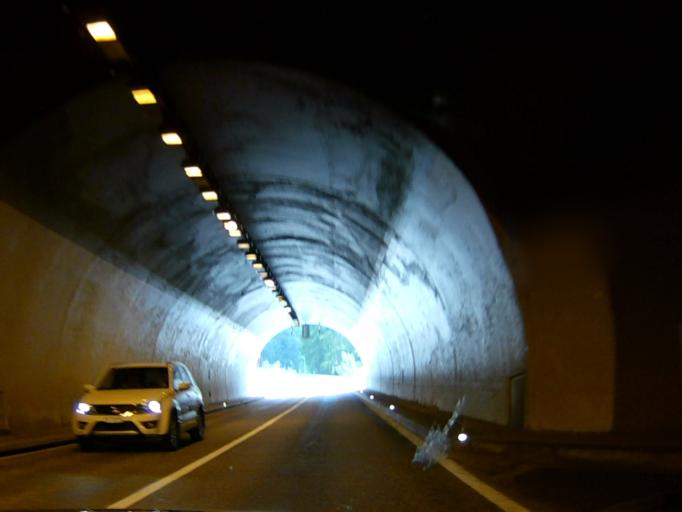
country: CH
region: Grisons
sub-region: Albula District
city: Tiefencastel
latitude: 46.6337
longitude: 9.5863
